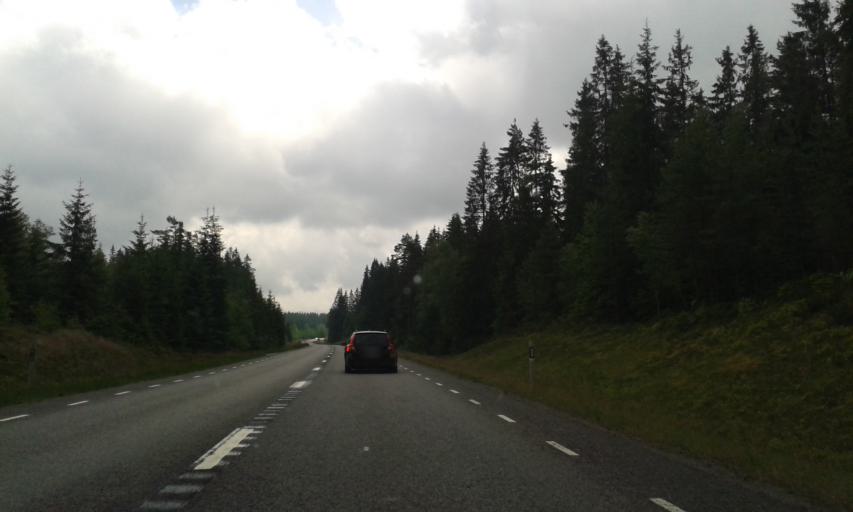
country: SE
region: Vaestra Goetaland
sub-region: Tranemo Kommun
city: Tranemo
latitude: 57.4414
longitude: 13.4284
